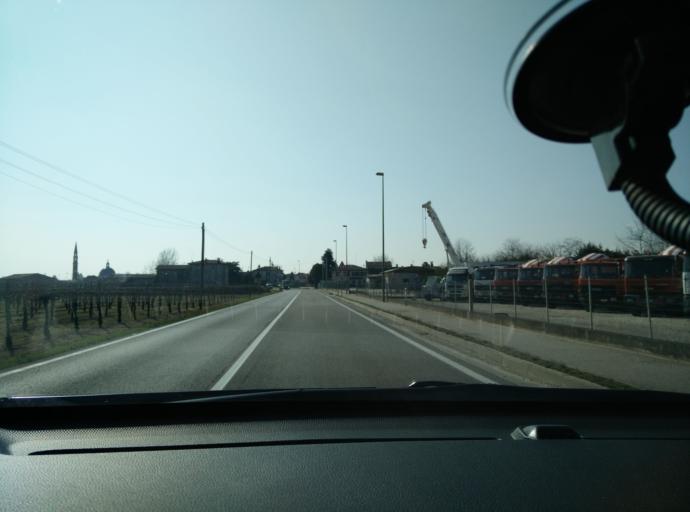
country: IT
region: Veneto
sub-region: Provincia di Treviso
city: San Michele di Piave
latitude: 45.8035
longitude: 12.3434
